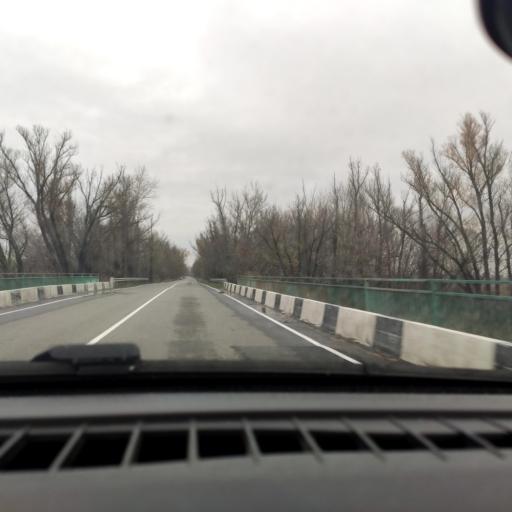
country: RU
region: Voronezj
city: Ostrogozhsk
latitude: 50.7705
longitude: 38.8876
